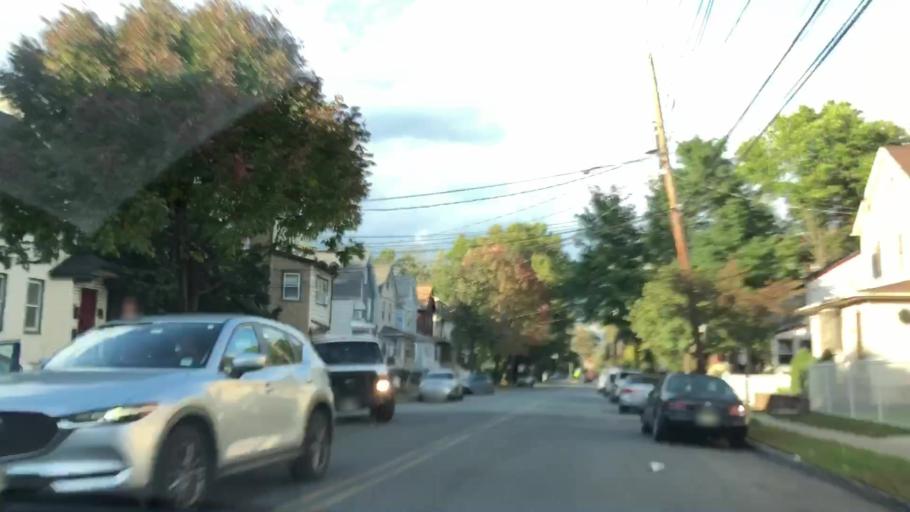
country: US
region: New Jersey
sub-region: Essex County
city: East Orange
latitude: 40.7845
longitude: -74.2044
